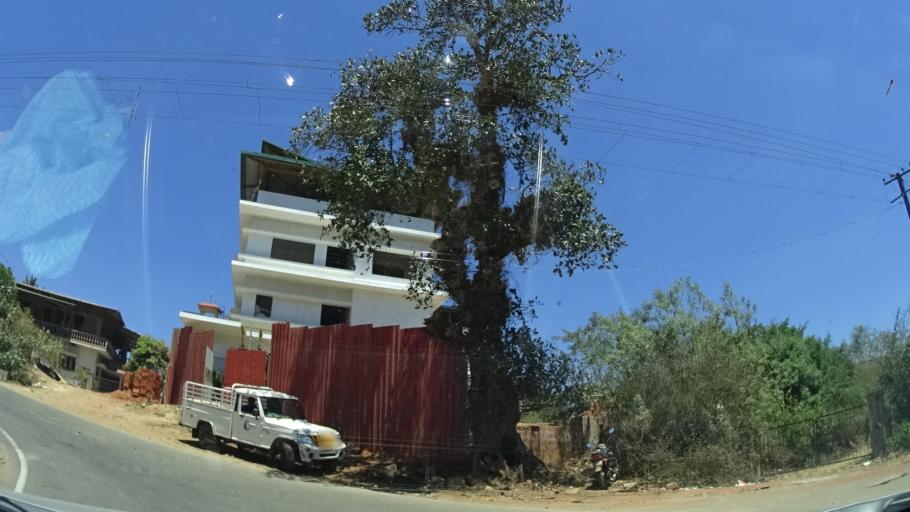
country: IN
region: Karnataka
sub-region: Chikmagalur
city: Sringeri
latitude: 13.2299
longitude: 75.3595
